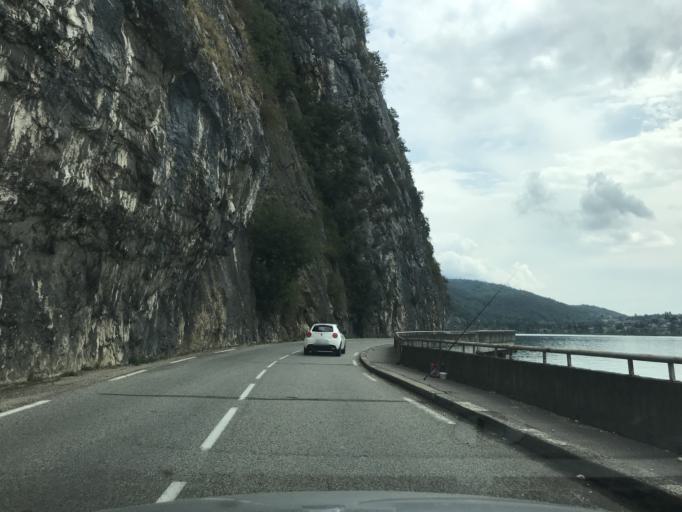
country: FR
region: Rhone-Alpes
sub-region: Departement de la Savoie
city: Brison-Saint-Innocent
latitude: 45.7467
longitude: 5.8846
